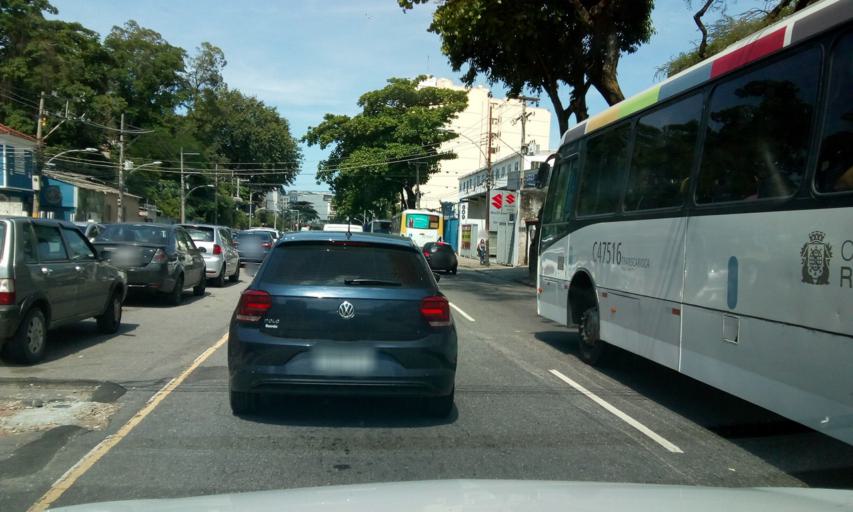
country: BR
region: Rio de Janeiro
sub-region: Rio De Janeiro
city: Rio de Janeiro
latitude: -22.9166
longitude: -43.2398
